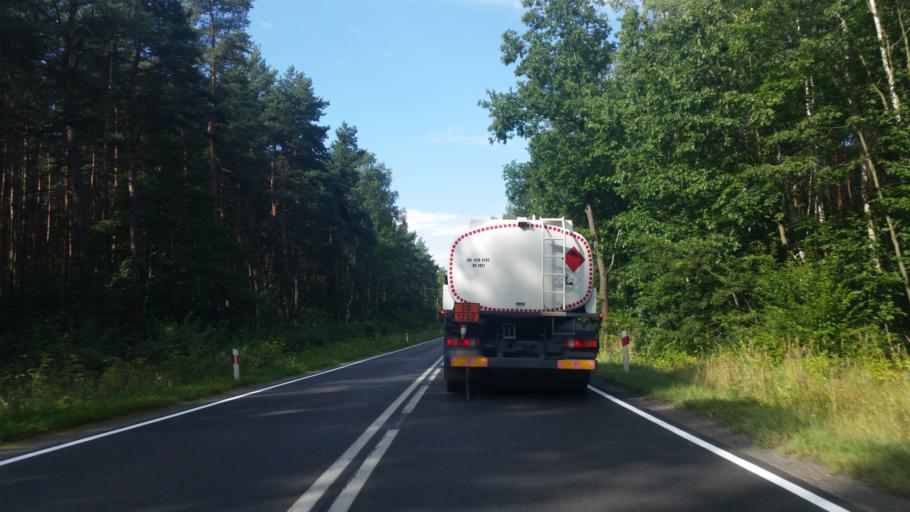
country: PL
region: Lesser Poland Voivodeship
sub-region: Powiat chrzanowski
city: Zarki
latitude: 50.1154
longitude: 19.3540
